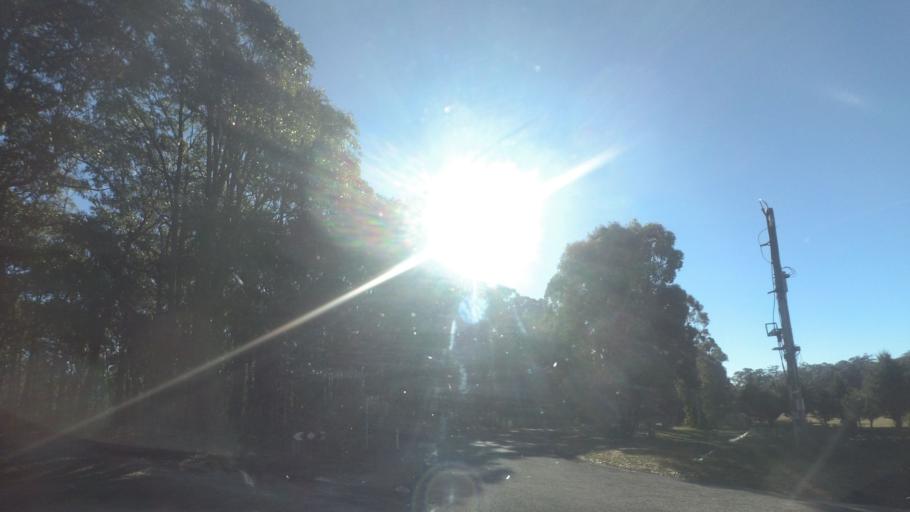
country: AU
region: Victoria
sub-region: Mount Alexander
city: Castlemaine
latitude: -37.3271
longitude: 144.3176
